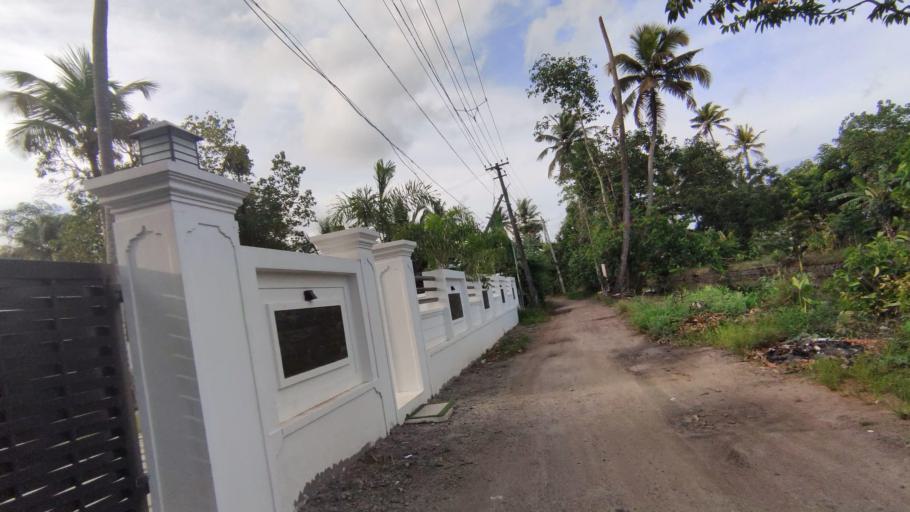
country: IN
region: Kerala
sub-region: Kottayam
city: Kottayam
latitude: 9.5997
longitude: 76.4398
